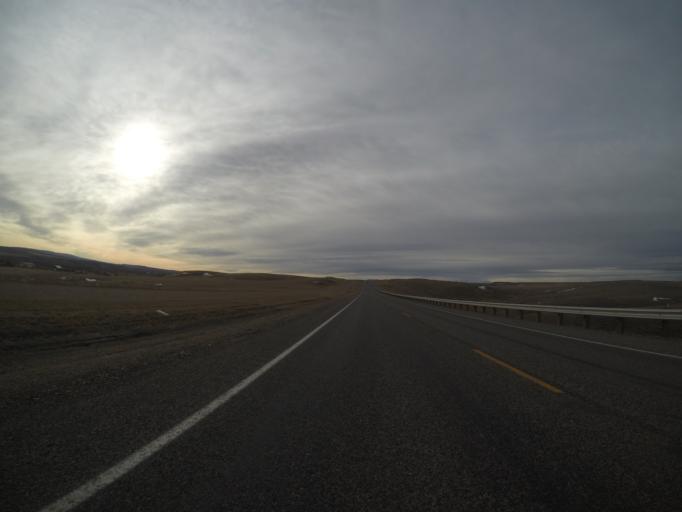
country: US
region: Montana
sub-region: Yellowstone County
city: Laurel
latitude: 45.5718
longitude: -108.8479
